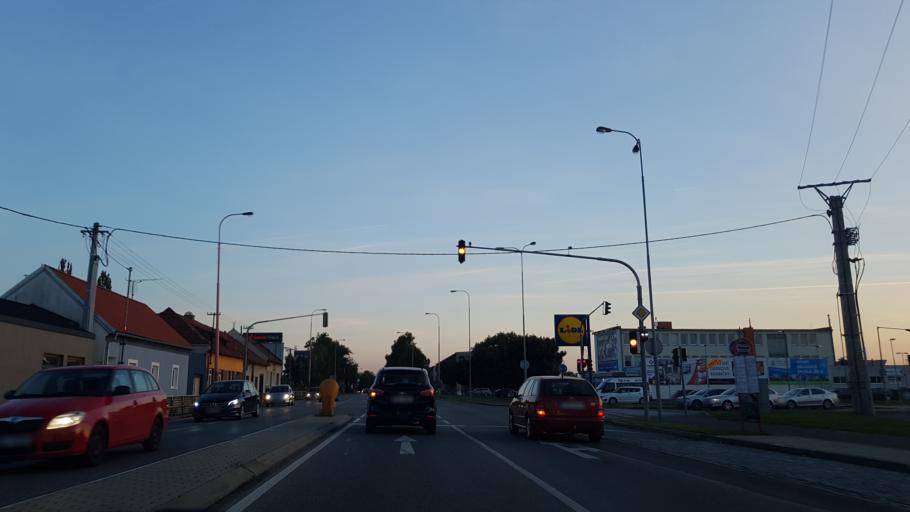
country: CZ
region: Zlin
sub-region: Okres Uherske Hradiste
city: Uherske Hradiste
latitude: 49.0588
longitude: 17.4665
